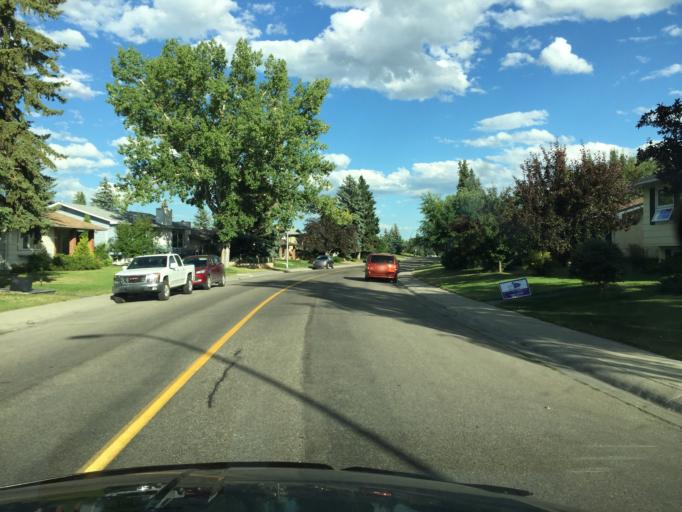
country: CA
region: Alberta
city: Calgary
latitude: 50.9373
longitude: -114.0465
